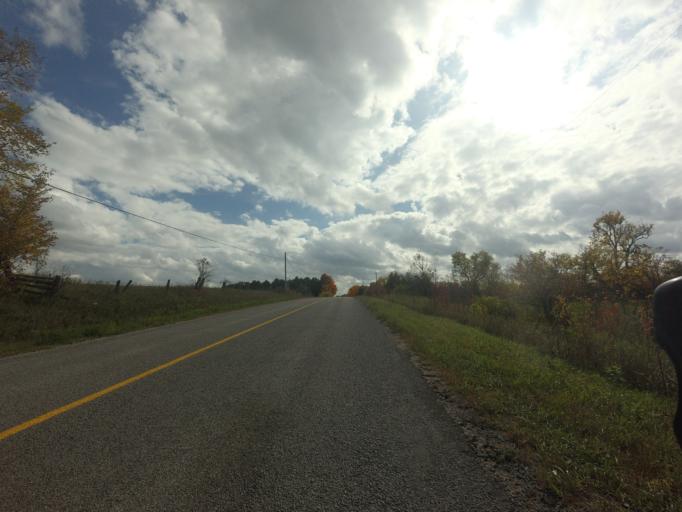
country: CA
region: Ontario
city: Pembroke
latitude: 45.5757
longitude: -77.1293
